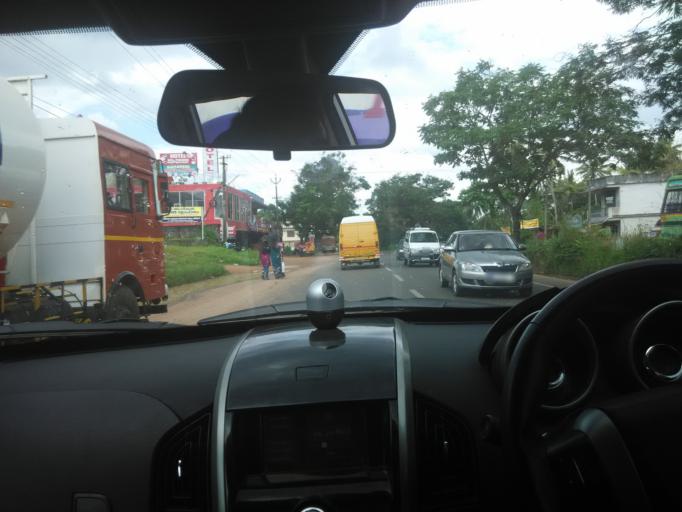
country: IN
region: Kerala
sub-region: Thiruvananthapuram
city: Attingal
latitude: 8.6429
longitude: 76.8436
